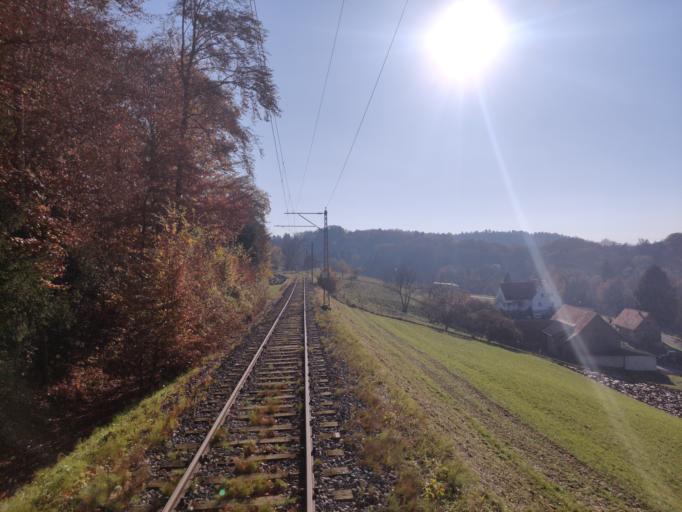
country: AT
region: Styria
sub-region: Politischer Bezirk Suedoststeiermark
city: Maierdorf
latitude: 46.9121
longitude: 15.8389
